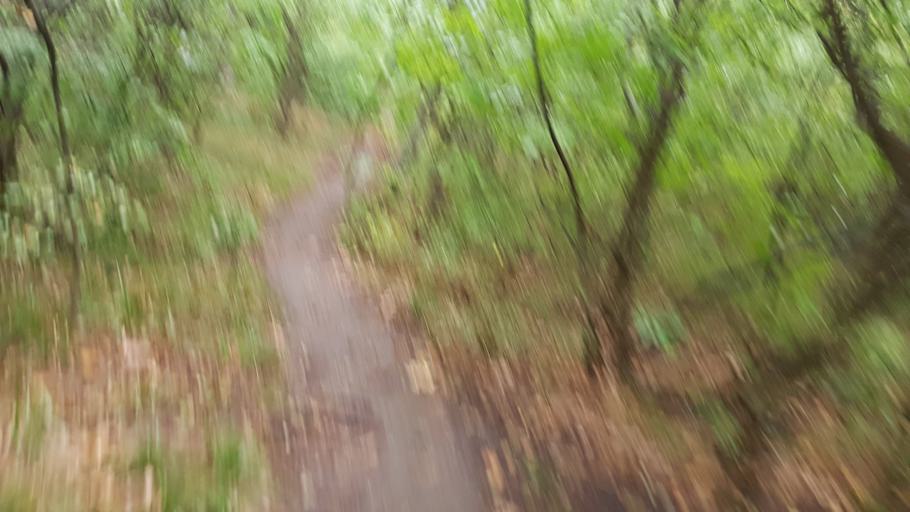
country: HU
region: Pest
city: Toeroekbalint
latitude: 47.4638
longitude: 18.9175
